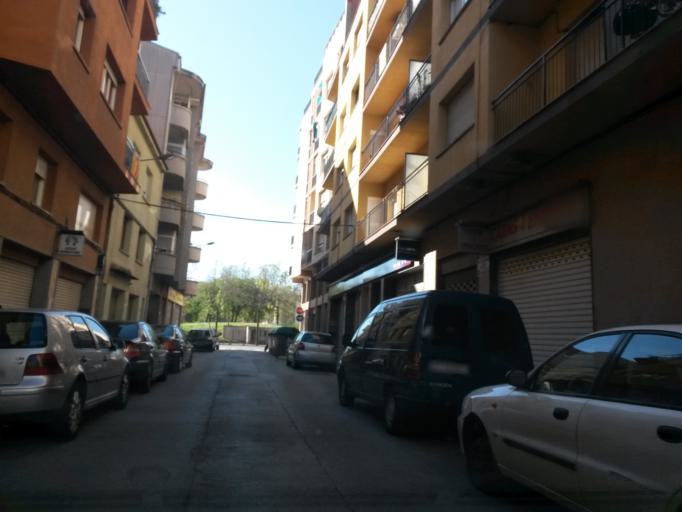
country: ES
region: Catalonia
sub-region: Provincia de Girona
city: Salt
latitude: 41.9755
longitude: 2.8051
